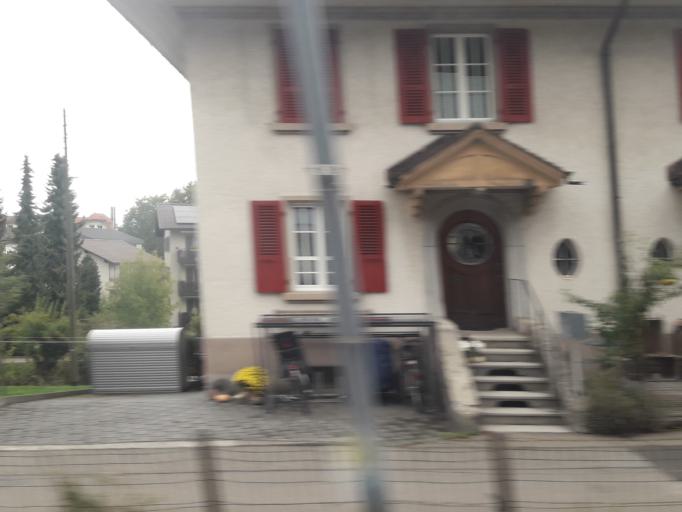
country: CH
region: Bern
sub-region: Bern-Mittelland District
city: Belp
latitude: 46.8910
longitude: 7.4971
